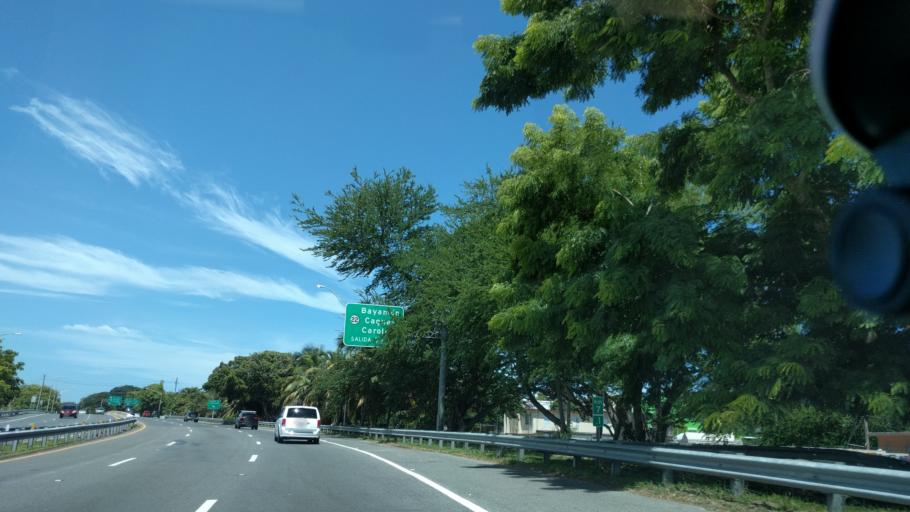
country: PR
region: San Juan
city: San Juan
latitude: 18.4396
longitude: -66.0636
